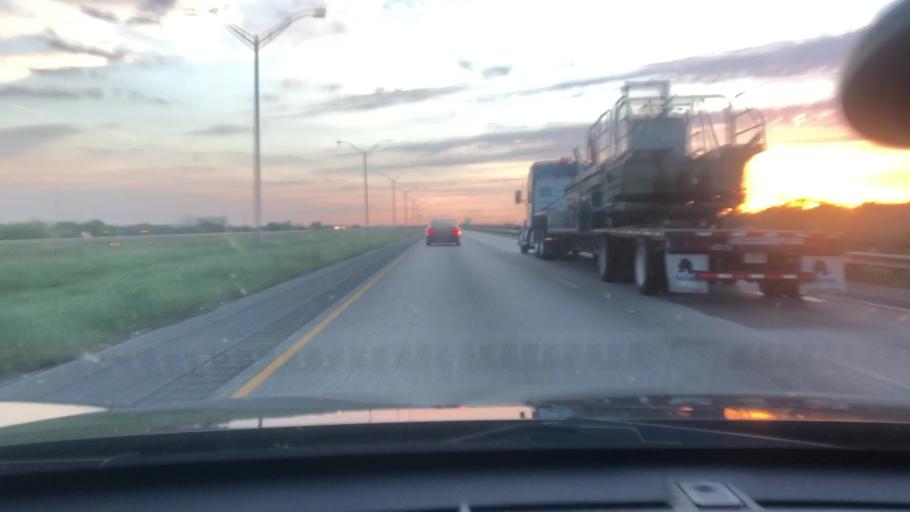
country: US
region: Texas
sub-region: Jackson County
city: Edna
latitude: 28.9853
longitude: -96.6539
